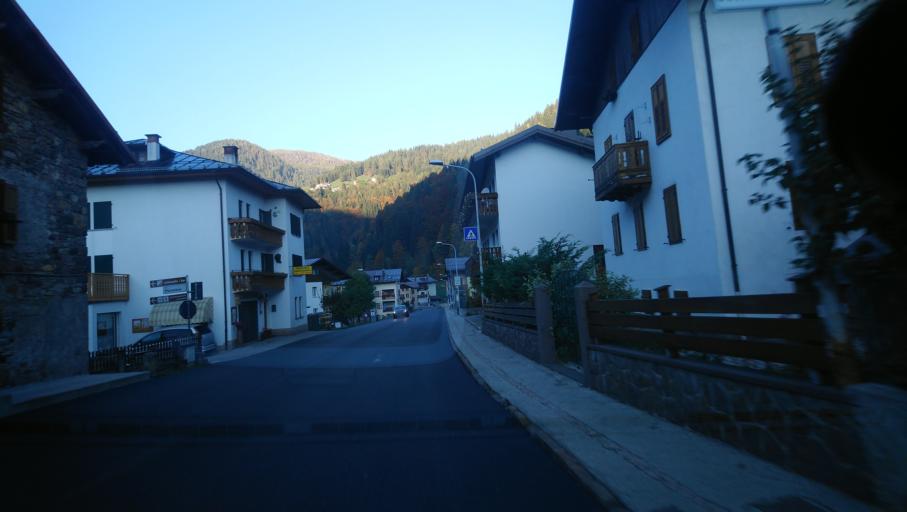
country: IT
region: Veneto
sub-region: Provincia di Belluno
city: Pie' Falcade
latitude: 46.3586
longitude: 11.8773
